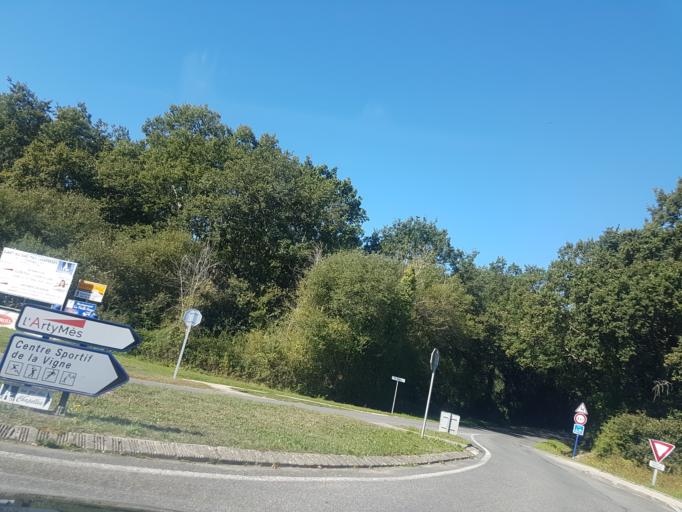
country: FR
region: Pays de la Loire
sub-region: Departement de la Loire-Atlantique
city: Mesquer
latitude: 47.3894
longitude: -2.4472
